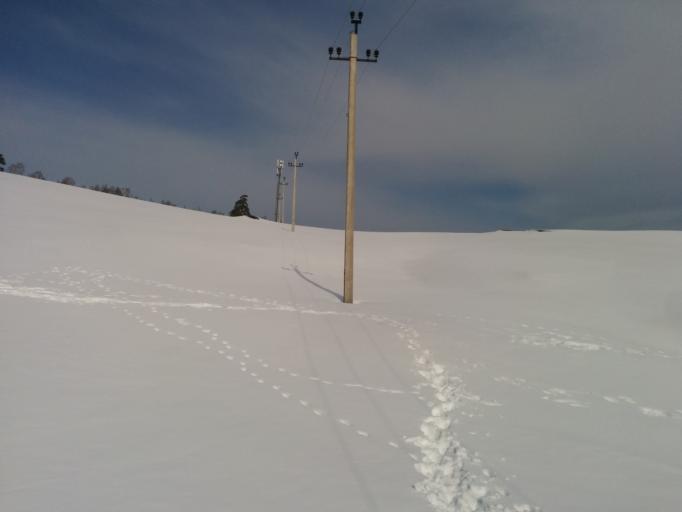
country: RU
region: Bashkortostan
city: Lomovka
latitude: 53.8059
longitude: 58.1955
